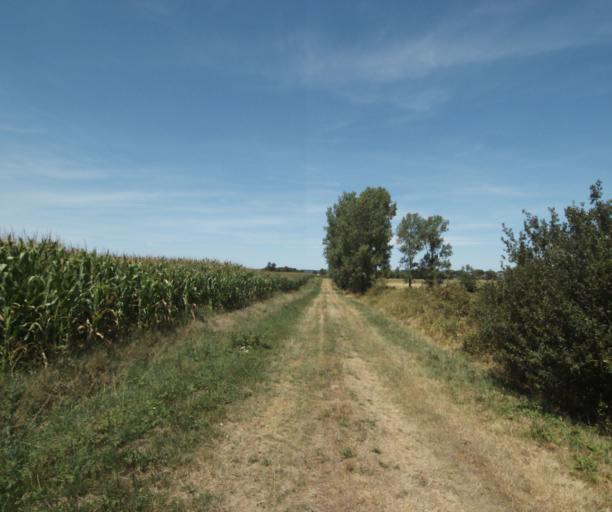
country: FR
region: Midi-Pyrenees
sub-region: Departement de la Haute-Garonne
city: Revel
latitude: 43.5018
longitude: 2.0303
